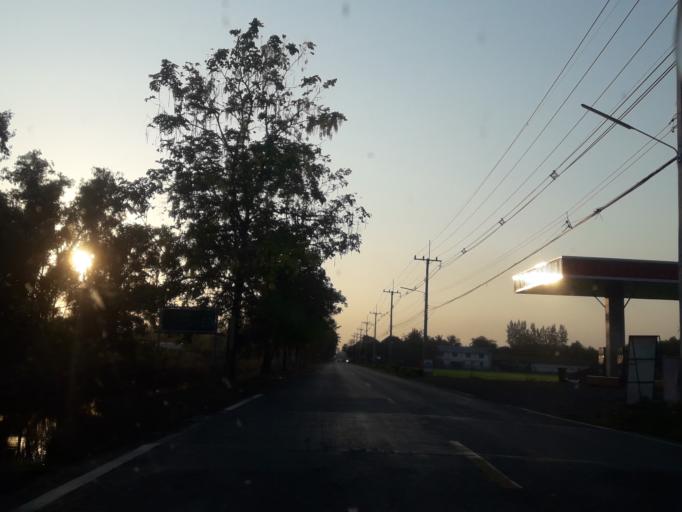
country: TH
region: Pathum Thani
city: Nong Suea
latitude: 14.1370
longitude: 100.8349
